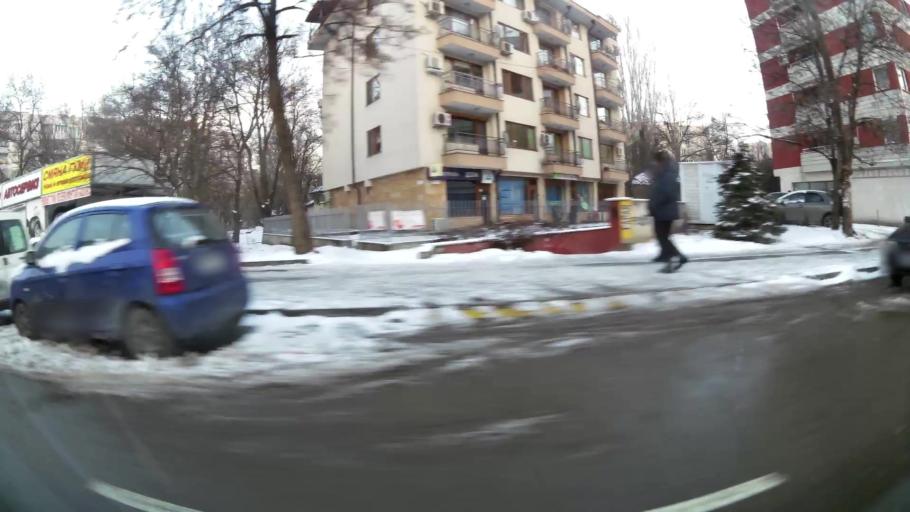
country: BG
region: Sofia-Capital
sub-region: Stolichna Obshtina
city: Sofia
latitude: 42.6825
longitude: 23.3723
